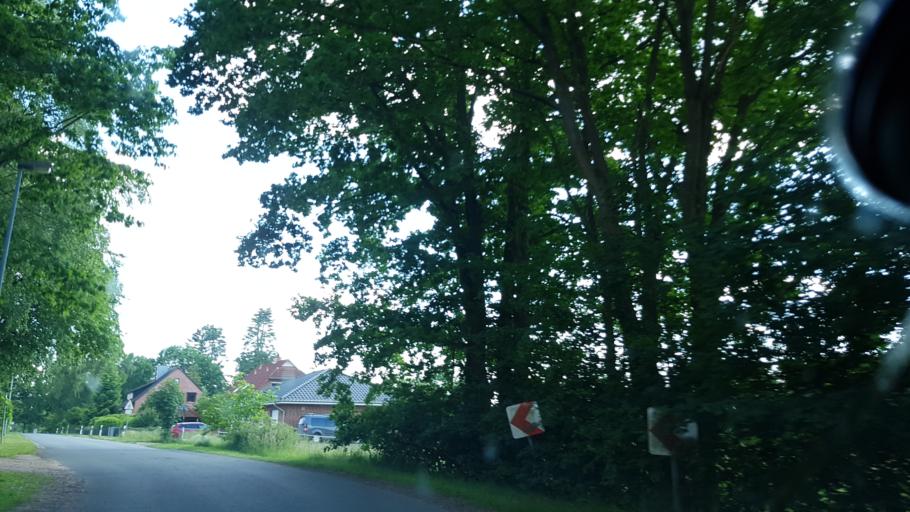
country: DE
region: Lower Saxony
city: Wenzendorf
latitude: 53.3537
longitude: 9.7694
